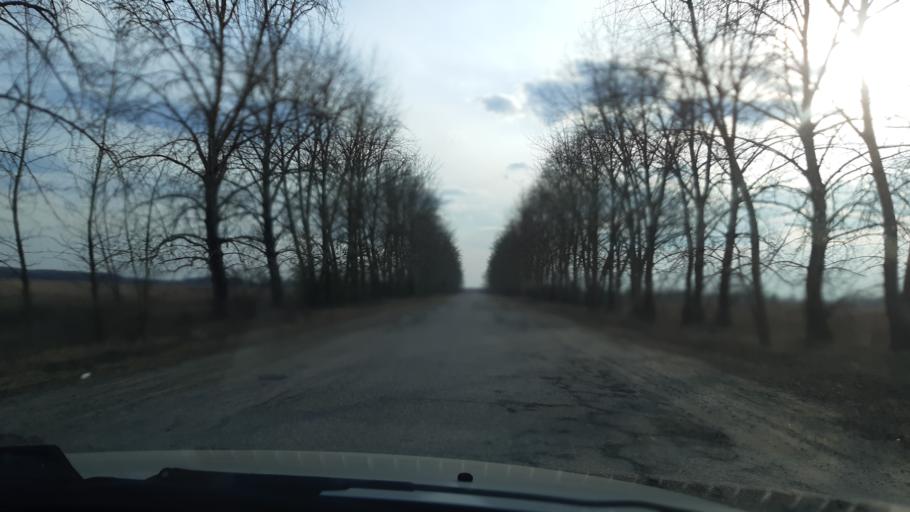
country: RU
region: Vladimir
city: Nikologory
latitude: 56.1036
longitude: 41.9772
